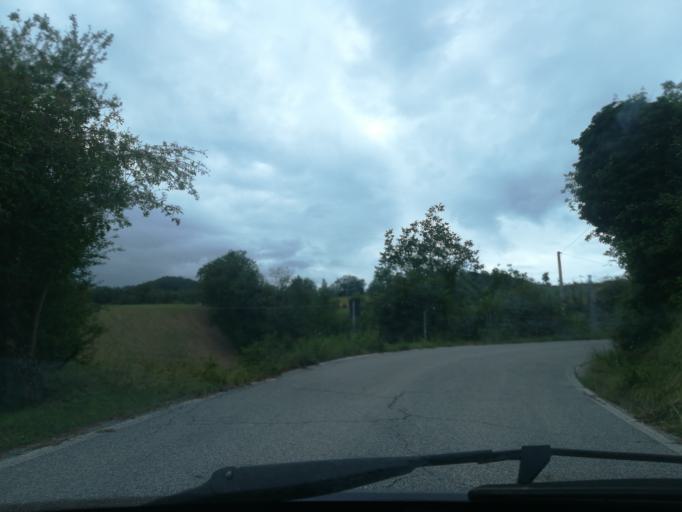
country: IT
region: The Marches
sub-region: Province of Fermo
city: Montefortino
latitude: 42.9372
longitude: 13.3734
